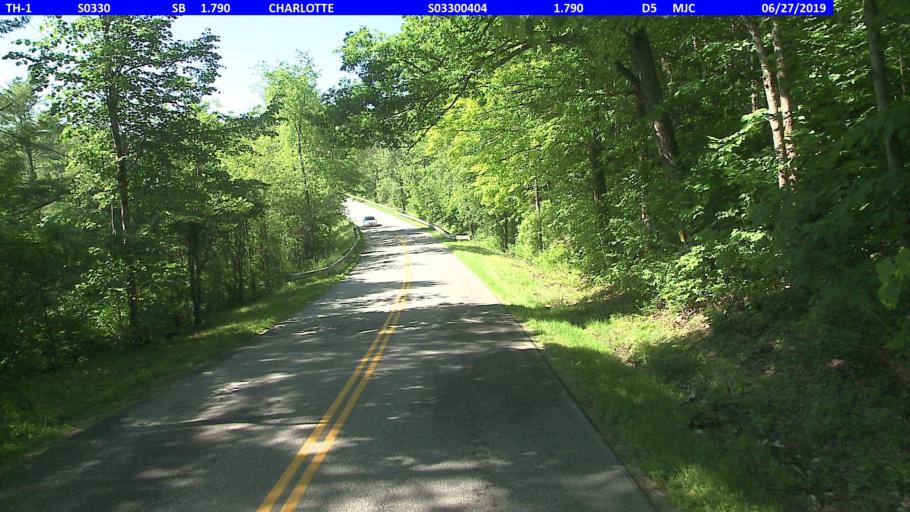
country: US
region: Vermont
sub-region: Chittenden County
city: Hinesburg
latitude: 44.3448
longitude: -73.1944
